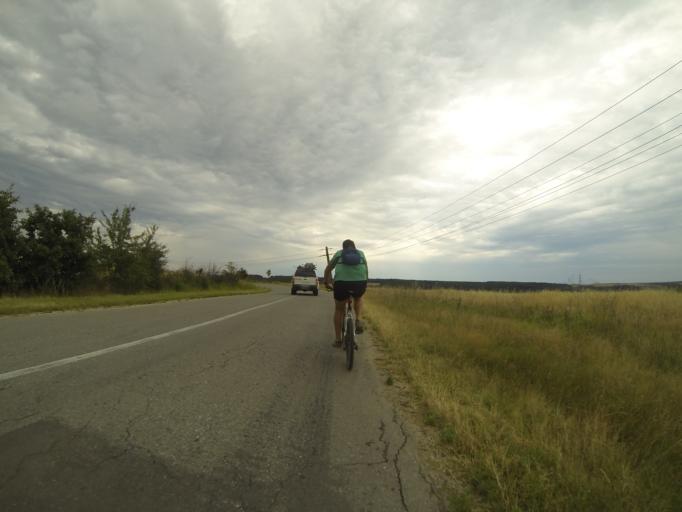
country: RO
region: Dolj
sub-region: Comuna Filiasi
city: Fratostita
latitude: 44.5740
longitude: 23.5872
